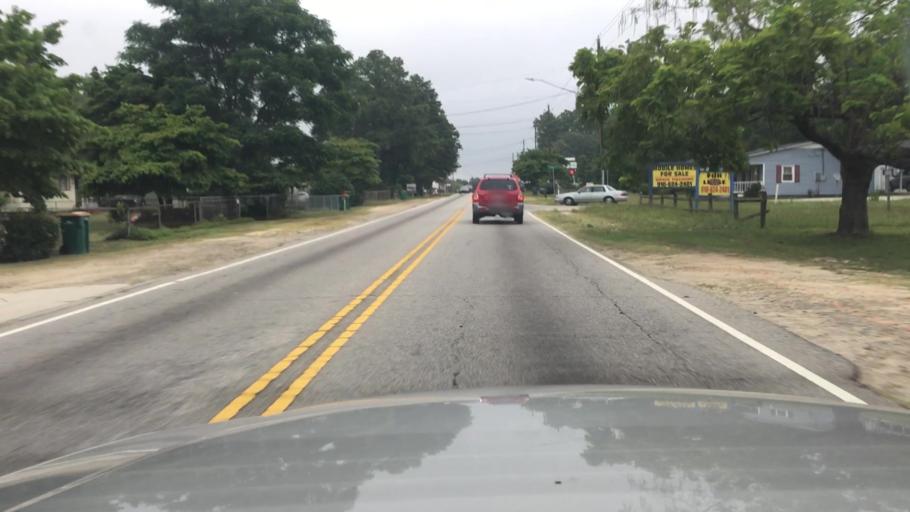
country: US
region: North Carolina
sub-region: Cumberland County
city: Hope Mills
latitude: 34.9836
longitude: -78.9698
